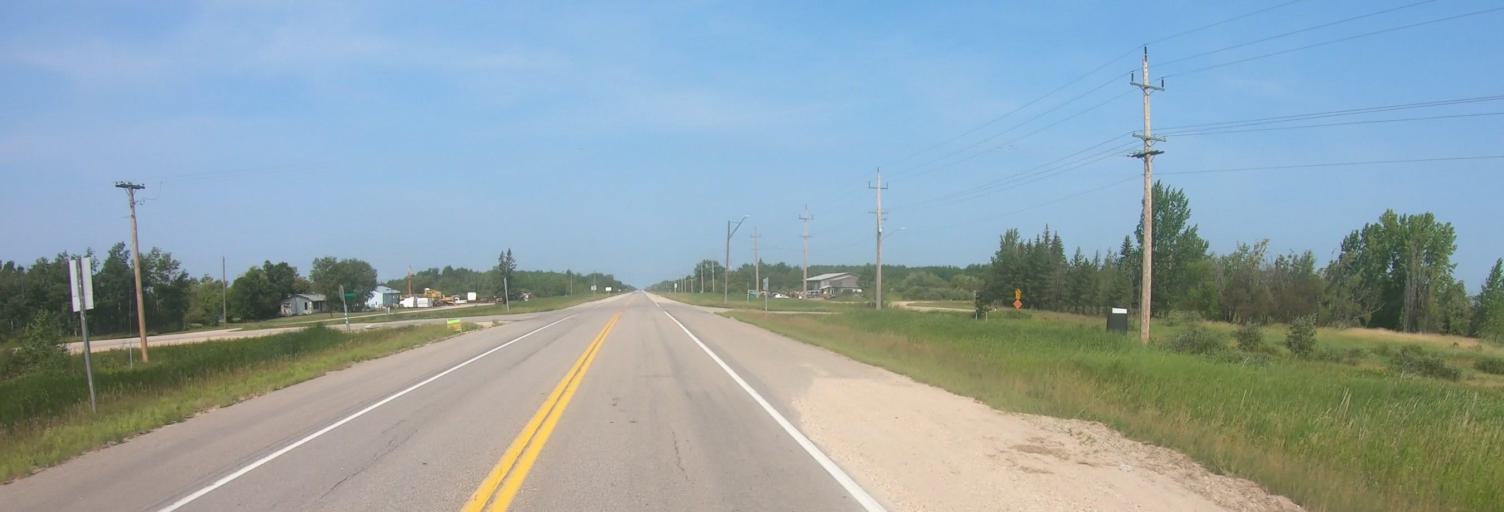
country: CA
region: Manitoba
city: La Broquerie
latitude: 49.2834
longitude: -96.5089
